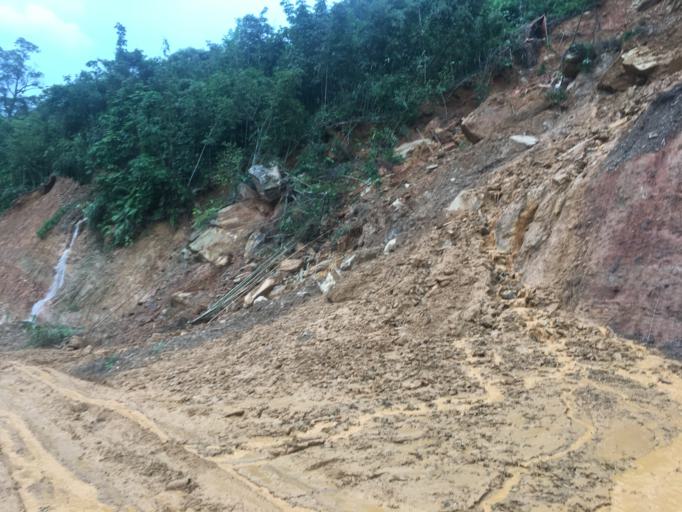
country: VN
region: Ha Giang
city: Thi Tran Tam Son
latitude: 22.9489
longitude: 105.0331
